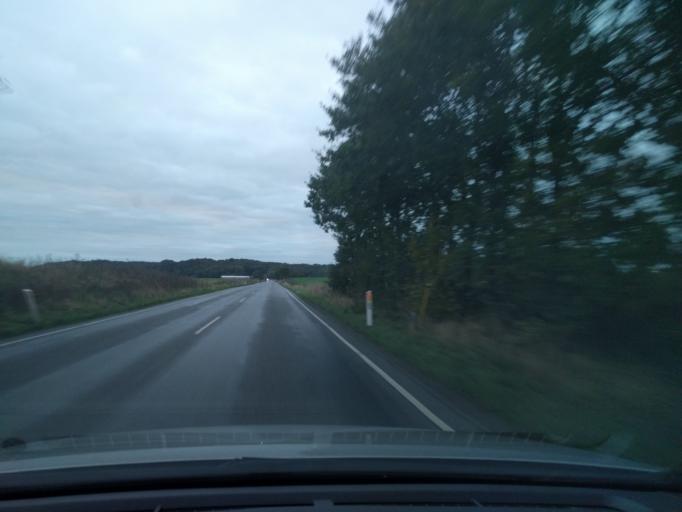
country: DK
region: South Denmark
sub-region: Odense Kommune
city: Bellinge
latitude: 55.2175
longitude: 10.3087
